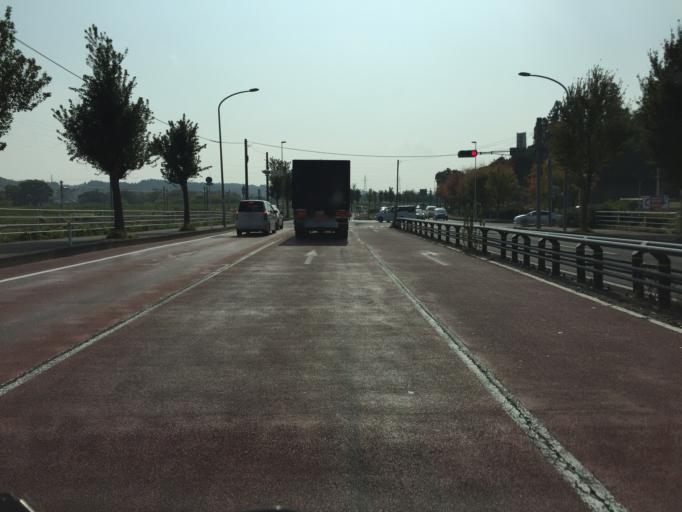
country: JP
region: Fukushima
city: Nihommatsu
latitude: 37.6002
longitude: 140.4622
